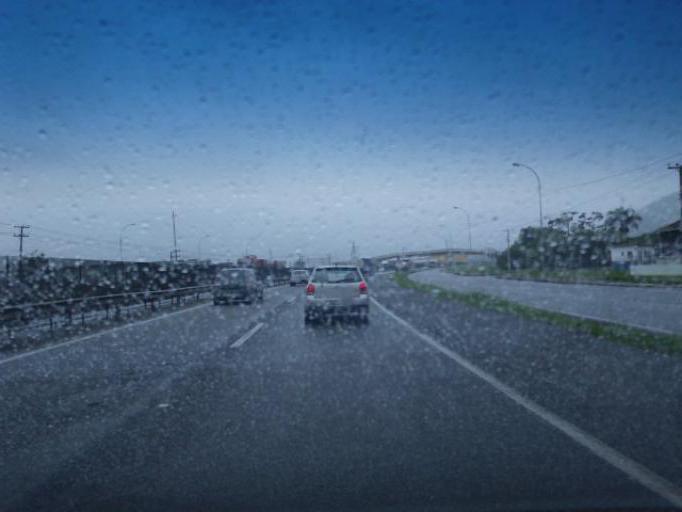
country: BR
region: Santa Catarina
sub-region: Itajai
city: Itajai
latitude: -26.8512
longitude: -48.7261
